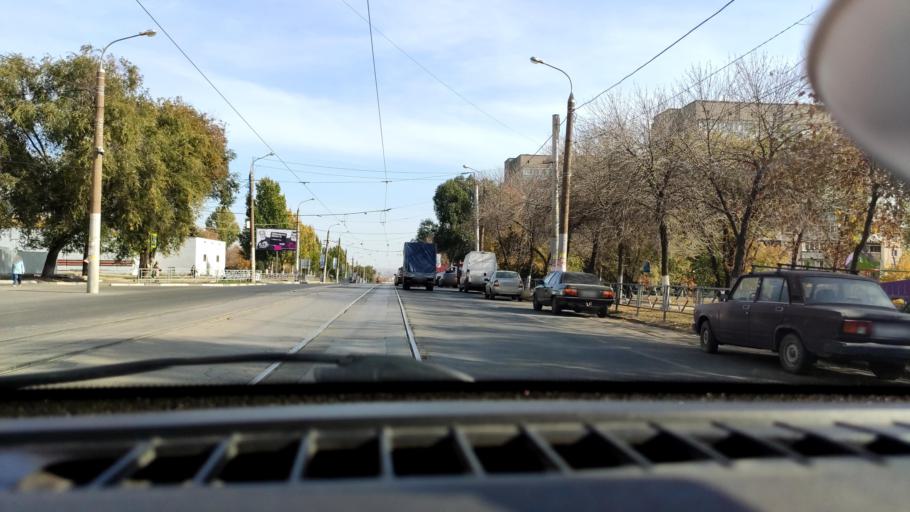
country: RU
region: Samara
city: Samara
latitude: 53.1919
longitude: 50.1987
